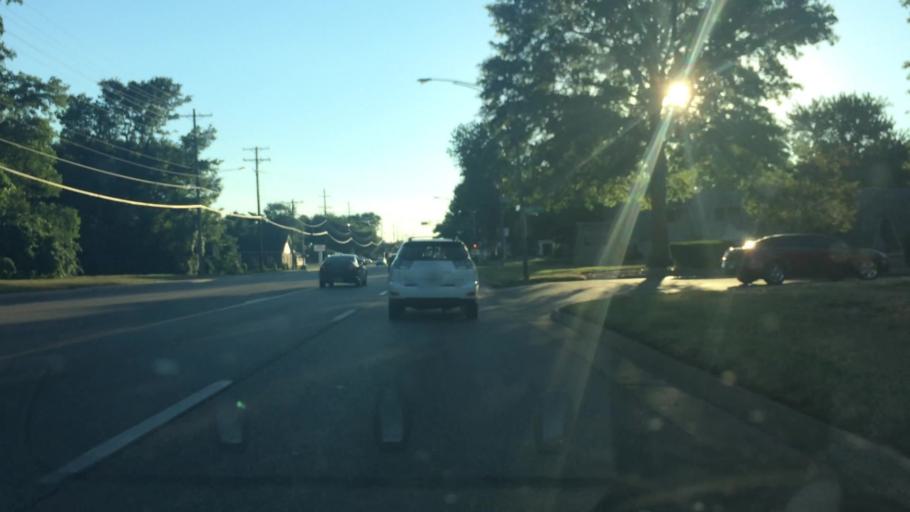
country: US
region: Missouri
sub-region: Greene County
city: Springfield
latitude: 37.1813
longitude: -93.2532
